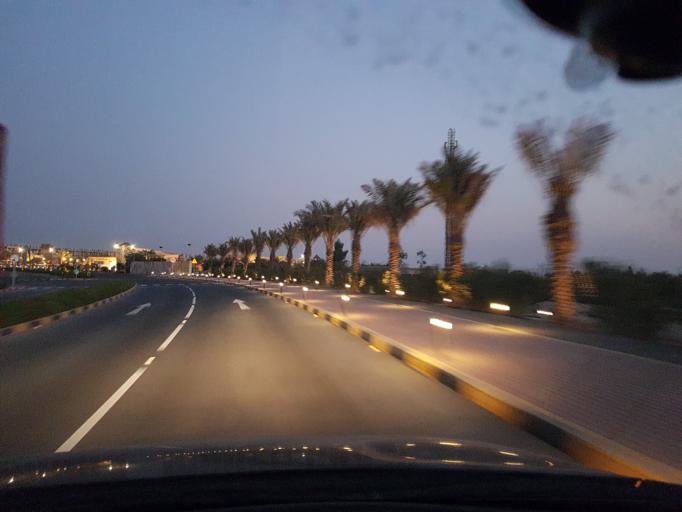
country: BH
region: Central Governorate
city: Dar Kulayb
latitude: 26.0172
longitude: 50.5088
